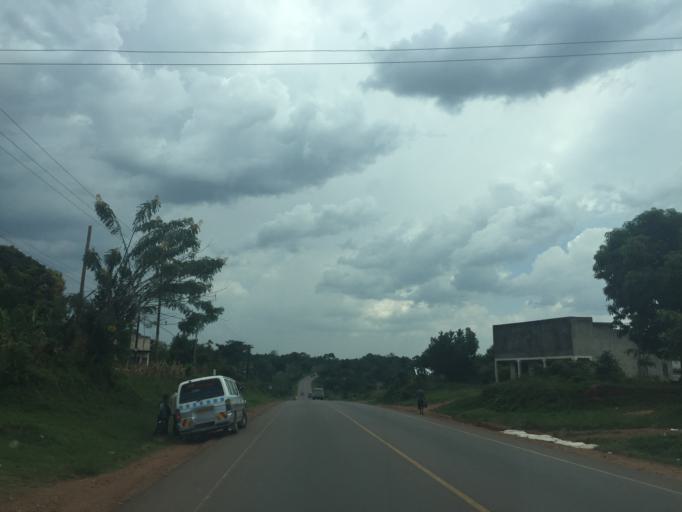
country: UG
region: Central Region
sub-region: Luwero District
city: Wobulenzi
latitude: 0.6777
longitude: 32.5264
